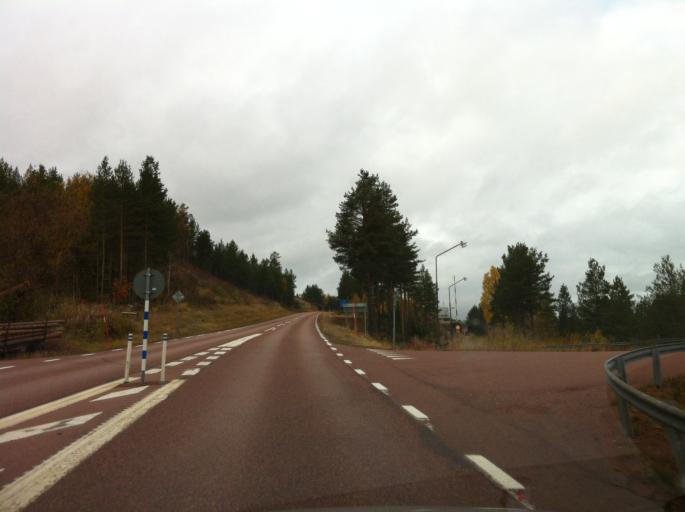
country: SE
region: Dalarna
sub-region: Alvdalens Kommun
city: AElvdalen
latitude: 61.2799
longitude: 13.7658
